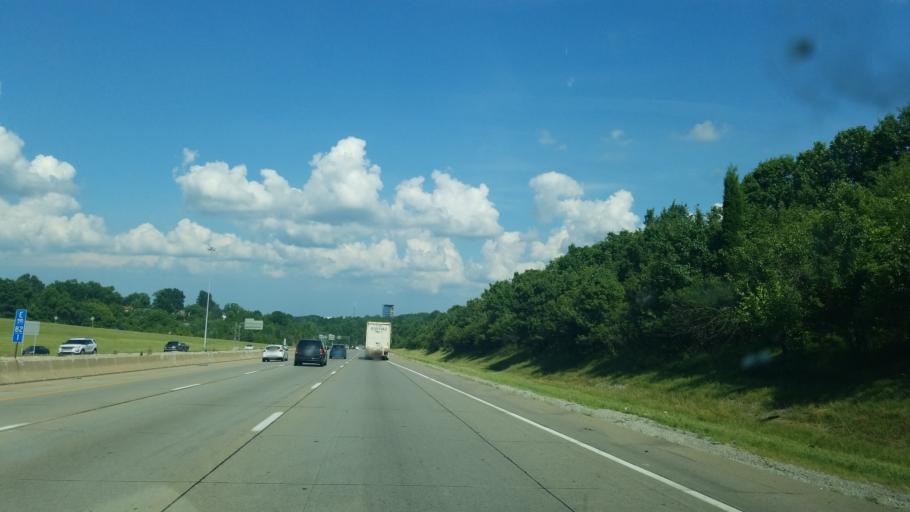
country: US
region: Kentucky
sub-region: Kenton County
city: Lakeside Park
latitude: 39.0261
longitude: -84.5691
